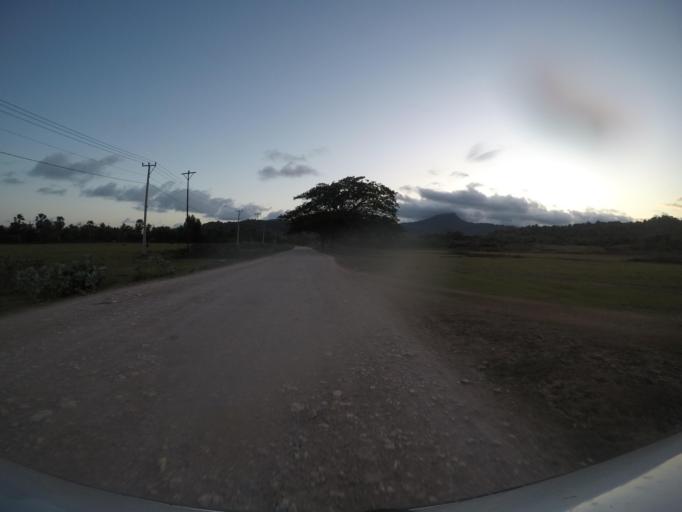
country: TL
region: Viqueque
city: Viqueque
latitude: -8.7709
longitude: 126.6417
